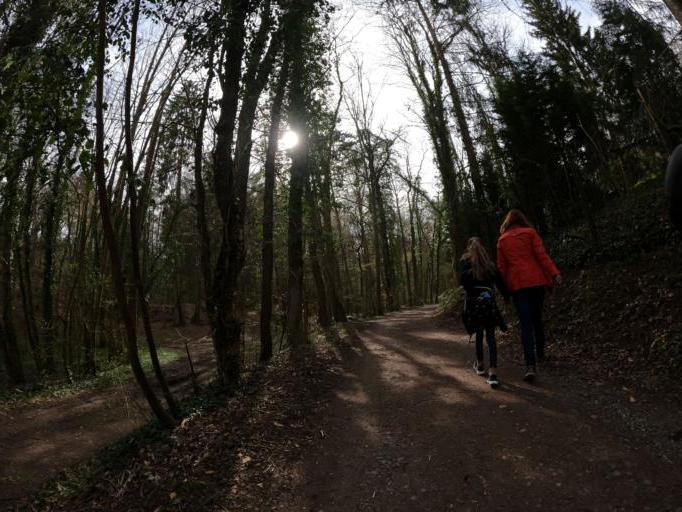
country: DE
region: Baden-Wuerttemberg
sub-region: Regierungsbezirk Stuttgart
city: Stuttgart-Ost
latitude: 48.7573
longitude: 9.2148
